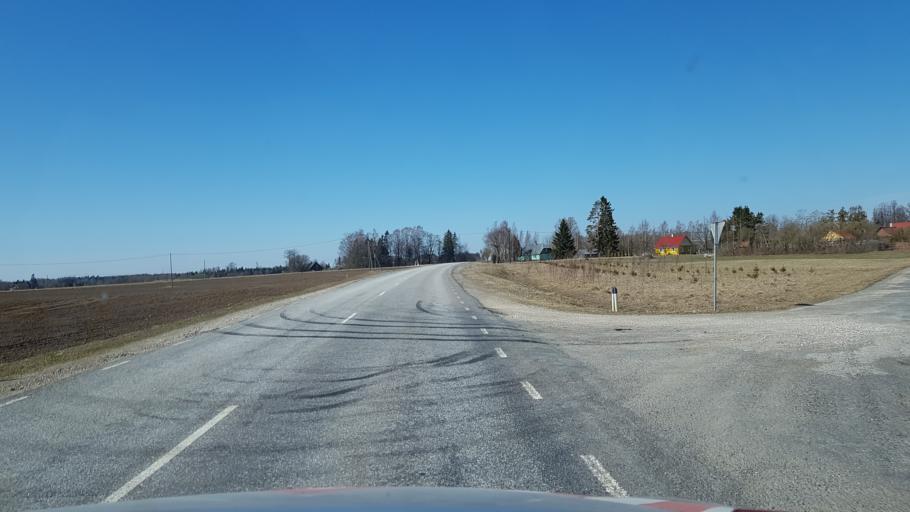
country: EE
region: Laeaene-Virumaa
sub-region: Vaeike-Maarja vald
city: Vaike-Maarja
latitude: 59.1425
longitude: 26.2349
